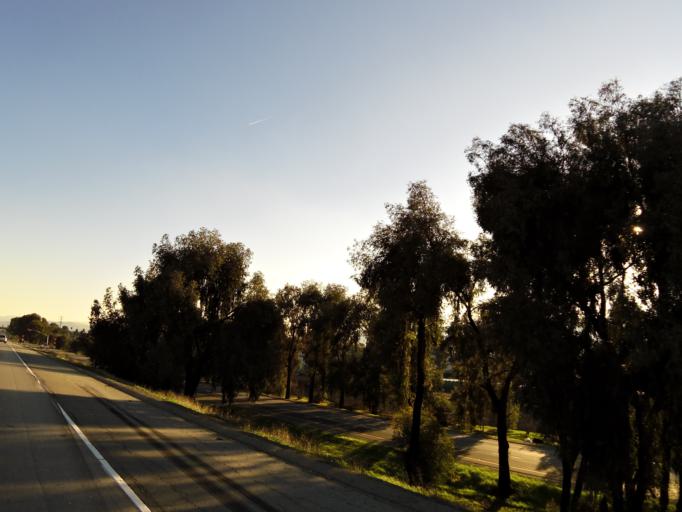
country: US
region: California
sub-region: Santa Clara County
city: Gilroy
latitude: 37.0213
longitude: -121.5663
